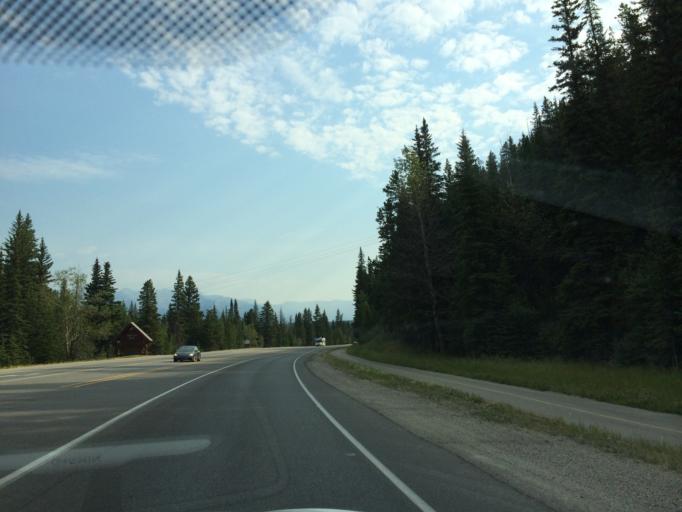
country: CA
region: Alberta
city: Banff
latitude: 51.1907
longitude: -115.5485
